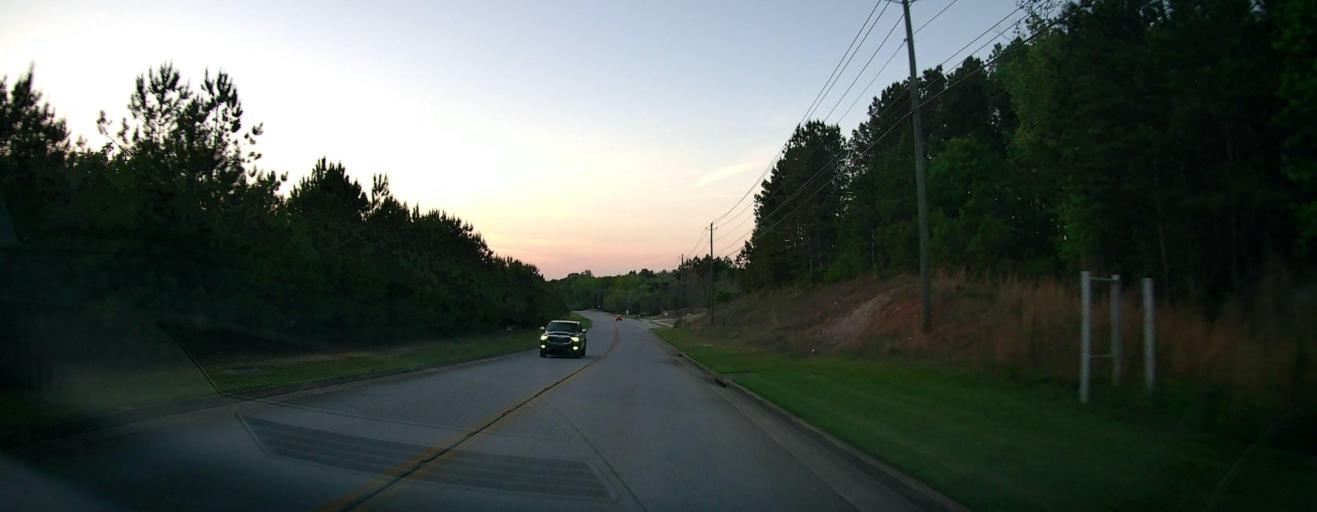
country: US
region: Georgia
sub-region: Henry County
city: Stockbridge
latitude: 33.4962
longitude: -84.2195
